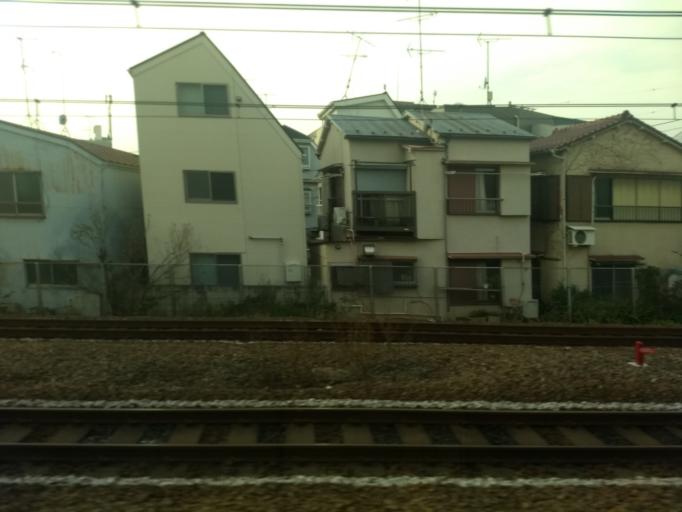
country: JP
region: Kanagawa
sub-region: Kawasaki-shi
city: Kawasaki
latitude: 35.5674
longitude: 139.7181
